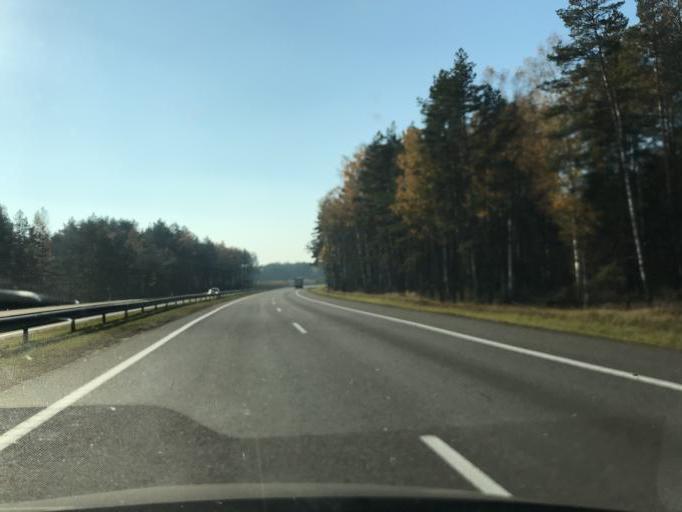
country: BY
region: Minsk
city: Enyerhyetykaw
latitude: 53.5534
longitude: 26.9656
